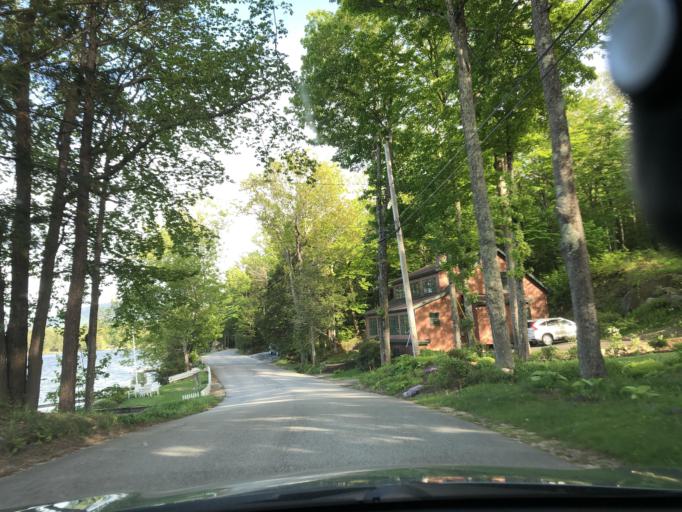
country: US
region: New Hampshire
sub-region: Merrimack County
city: New London
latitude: 43.4212
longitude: -71.9540
